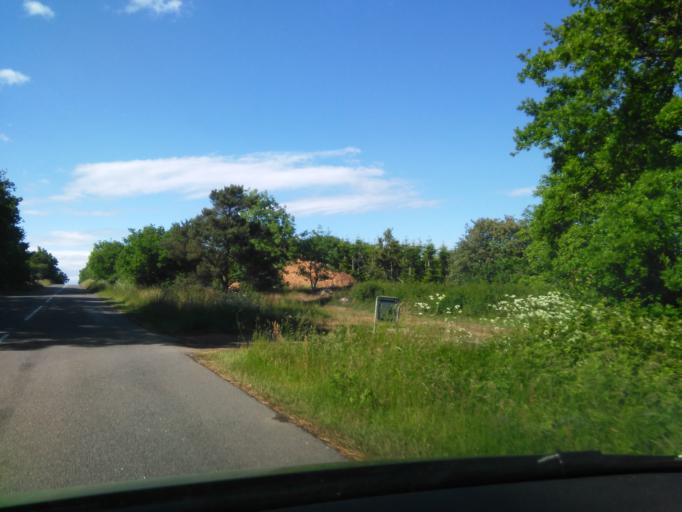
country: DK
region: Capital Region
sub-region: Bornholm Kommune
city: Nexo
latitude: 55.0680
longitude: 15.0831
